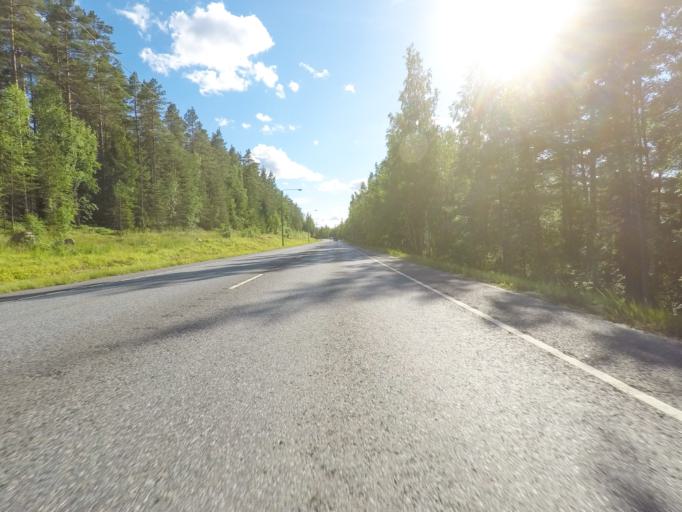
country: FI
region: Uusimaa
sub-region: Helsinki
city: Vihti
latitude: 60.3387
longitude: 24.2972
